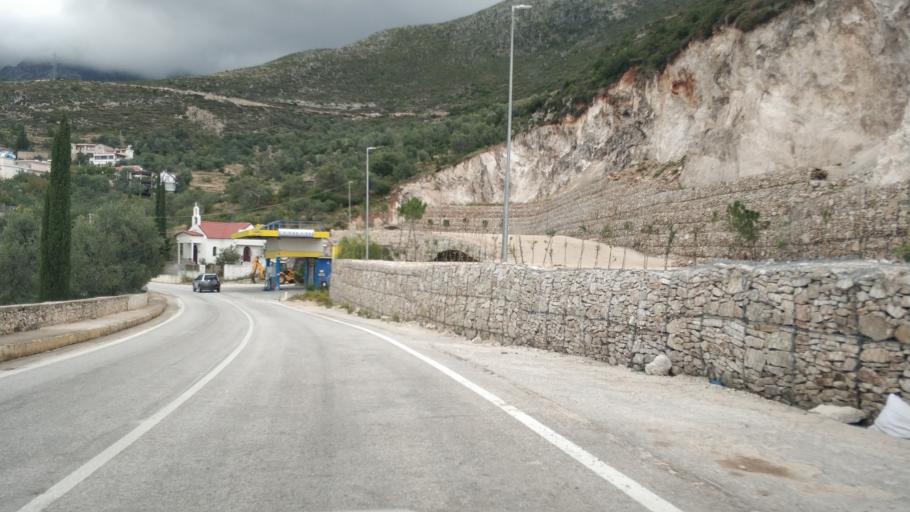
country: AL
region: Vlore
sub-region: Rrethi i Vlores
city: Vranisht
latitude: 40.1476
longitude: 19.6434
